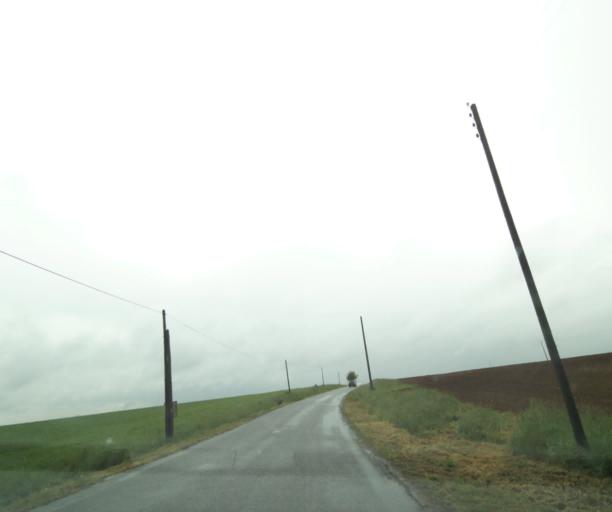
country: FR
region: Poitou-Charentes
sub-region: Departement de la Charente-Maritime
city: Corme-Royal
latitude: 45.7119
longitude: -0.8025
